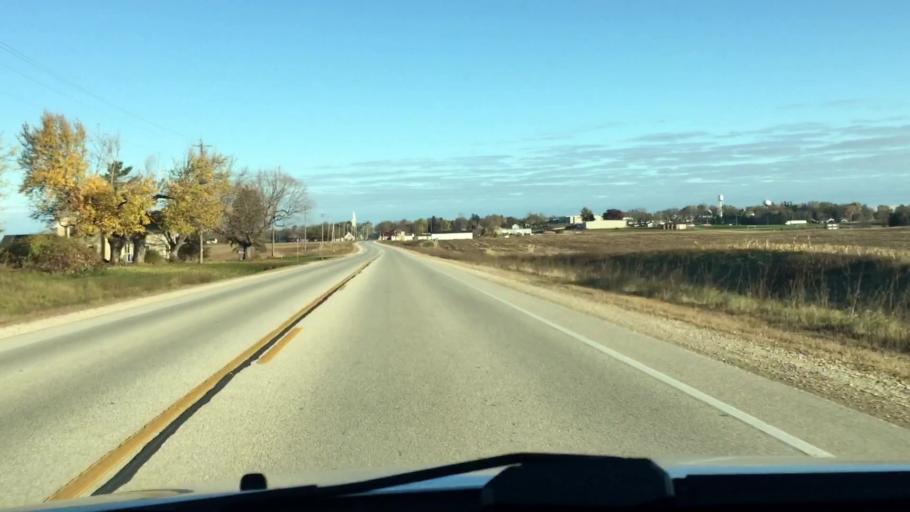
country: US
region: Wisconsin
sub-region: Dodge County
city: Lomira
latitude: 43.5785
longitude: -88.4499
